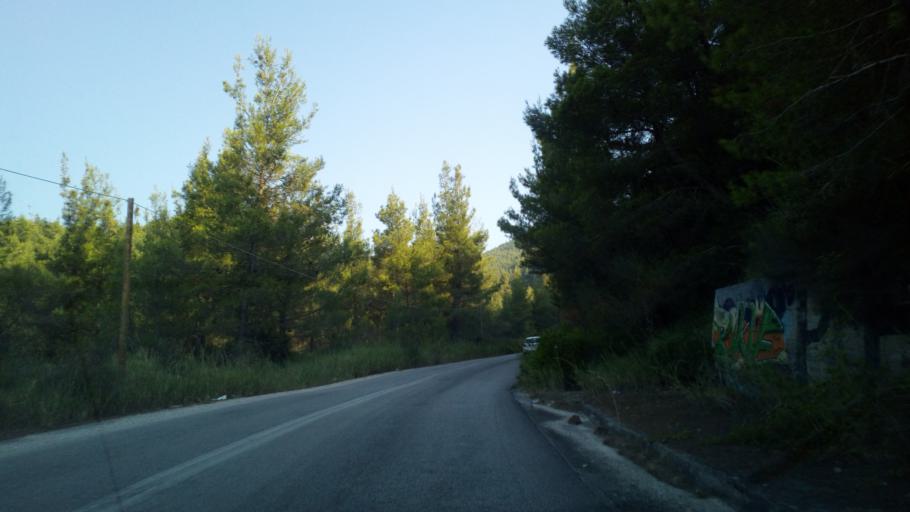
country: GR
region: Central Macedonia
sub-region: Nomos Chalkidikis
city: Neos Marmaras
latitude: 40.1768
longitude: 23.8349
